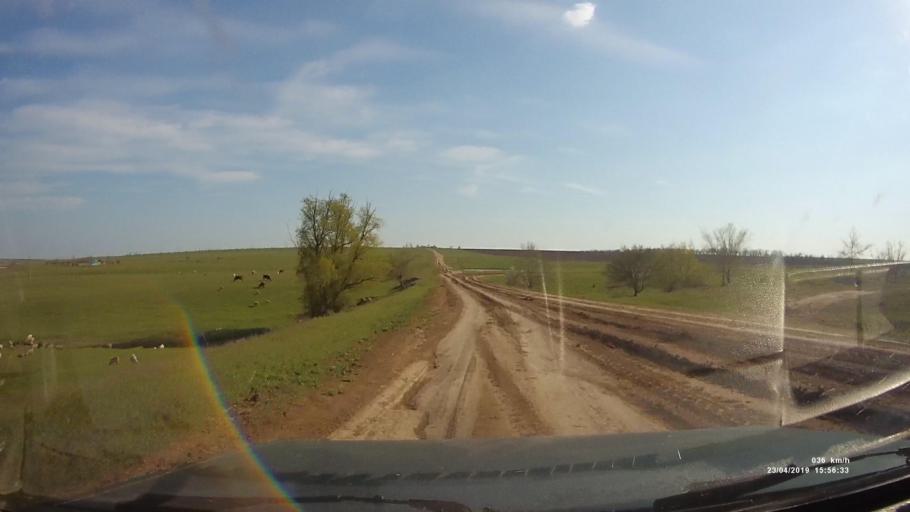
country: RU
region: Rostov
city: Remontnoye
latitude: 46.5364
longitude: 43.1111
